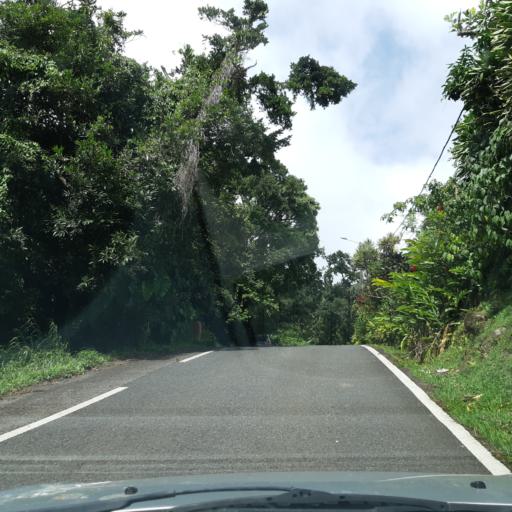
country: GP
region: Guadeloupe
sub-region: Guadeloupe
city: Saint-Claude
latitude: 16.0320
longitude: -61.6844
